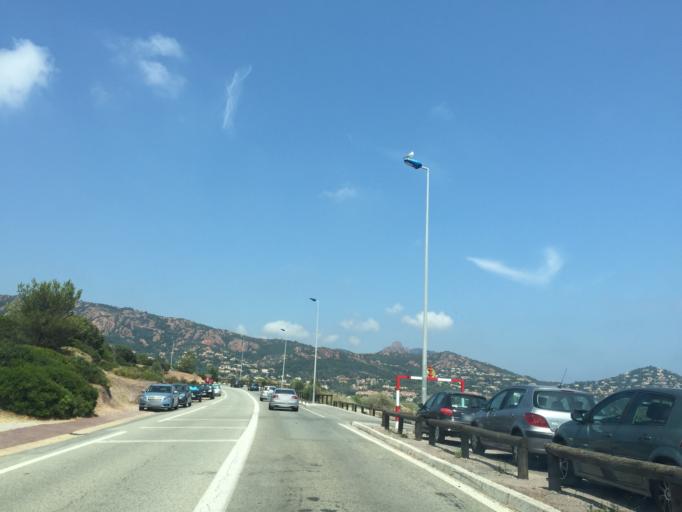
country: FR
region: Provence-Alpes-Cote d'Azur
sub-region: Departement du Var
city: Saint-Raphael
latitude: 43.4259
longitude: 6.8572
